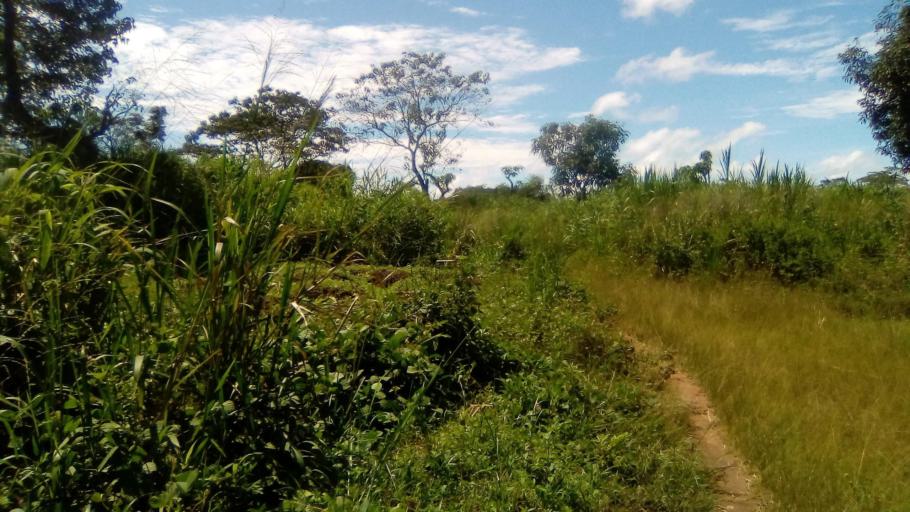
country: SL
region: Eastern Province
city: Simbakoro
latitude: 8.6320
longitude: -11.0016
